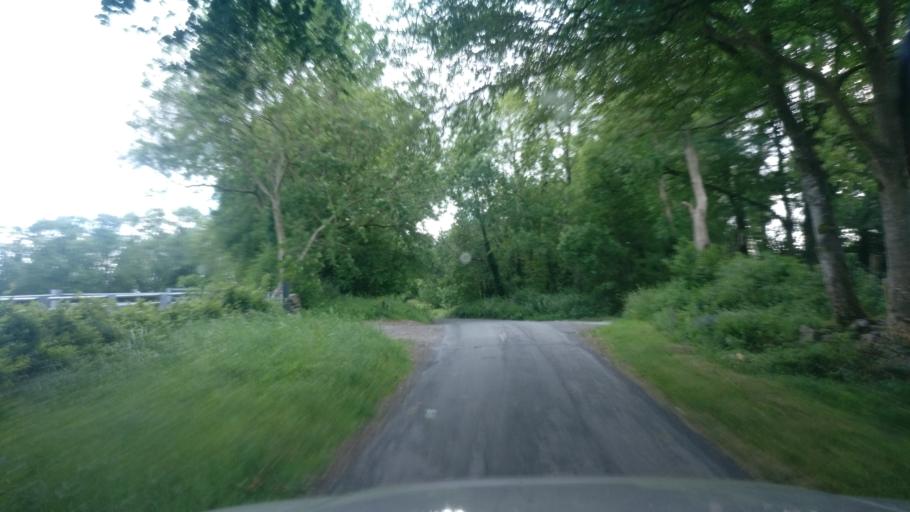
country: IE
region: Connaught
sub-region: County Galway
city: Ballinasloe
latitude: 53.2316
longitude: -8.2151
